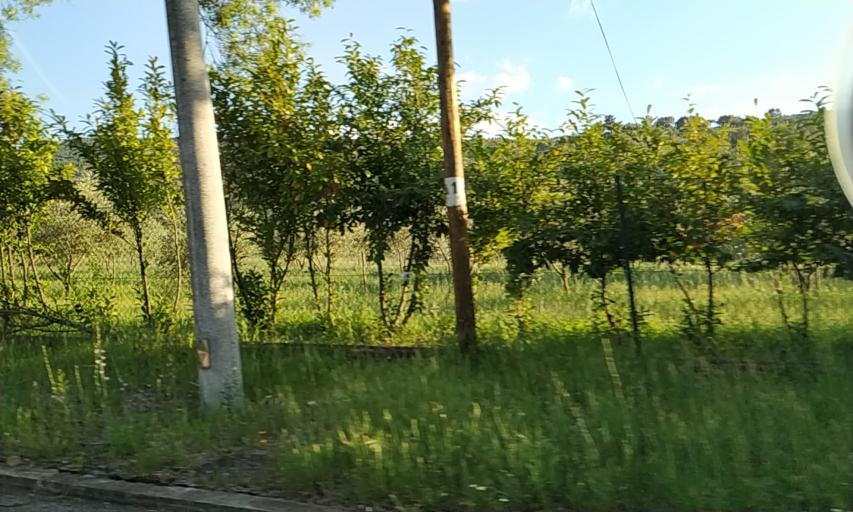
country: PT
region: Portalegre
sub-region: Portalegre
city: Sao Juliao
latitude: 39.3538
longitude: -7.3100
